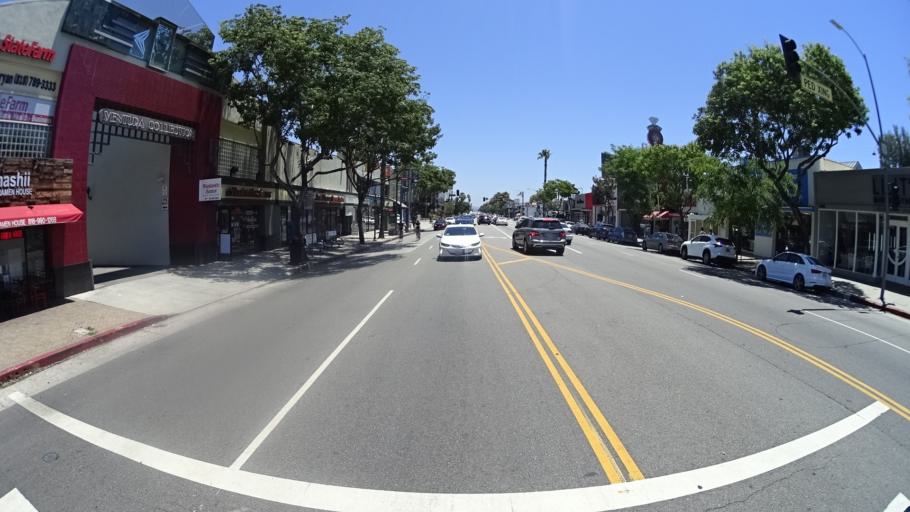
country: US
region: California
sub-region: Los Angeles County
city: Sherman Oaks
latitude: 34.1512
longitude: -118.4500
